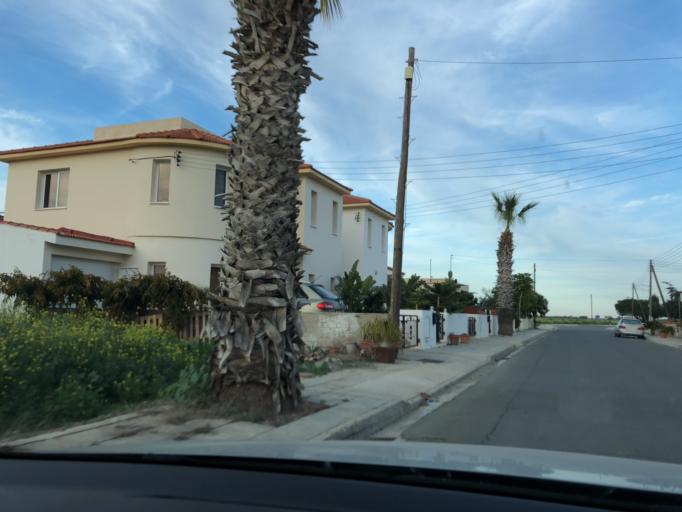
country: CY
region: Larnaka
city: Perivolia
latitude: 34.8276
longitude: 33.5840
